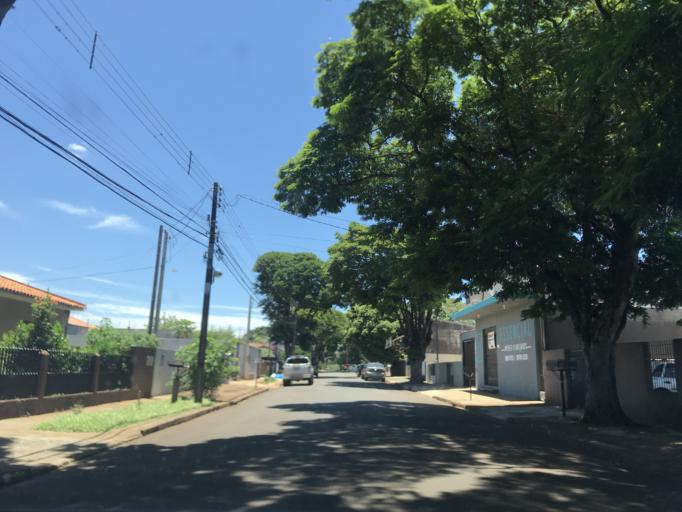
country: BR
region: Parana
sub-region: Sarandi
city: Sarandi
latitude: -23.4386
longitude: -51.8956
